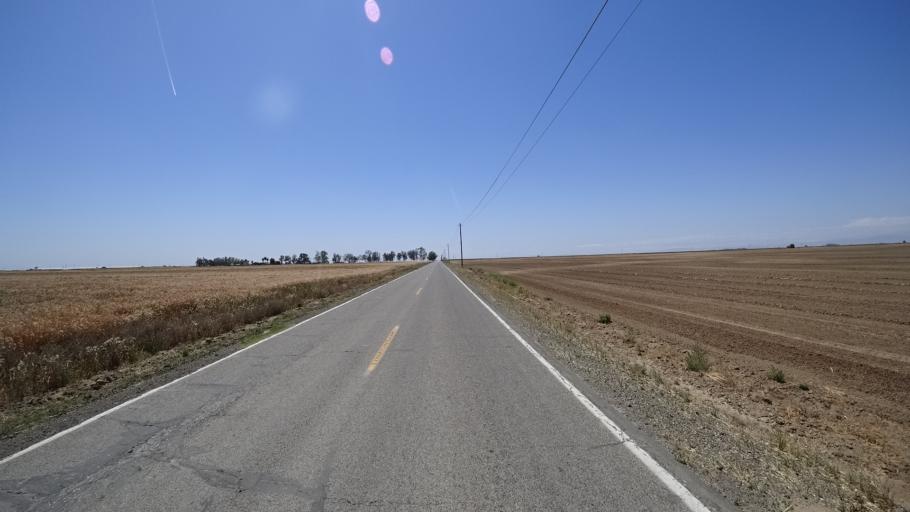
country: US
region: California
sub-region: Kings County
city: Armona
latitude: 36.2168
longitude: -119.7087
